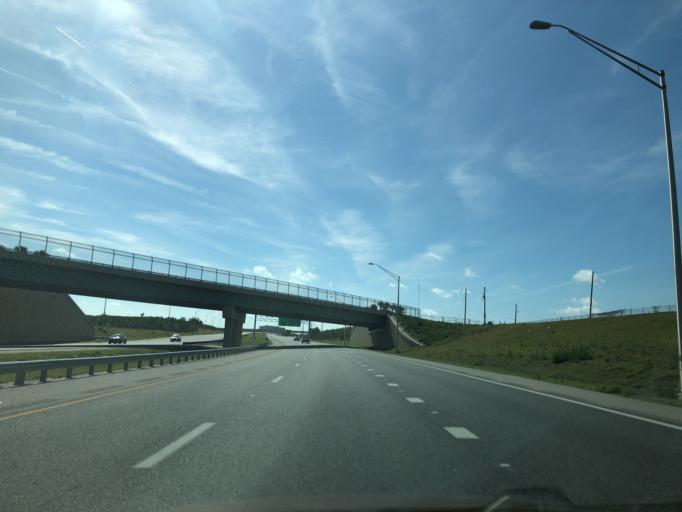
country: US
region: Florida
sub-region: Orange County
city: Paradise Heights
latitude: 28.6597
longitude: -81.5517
